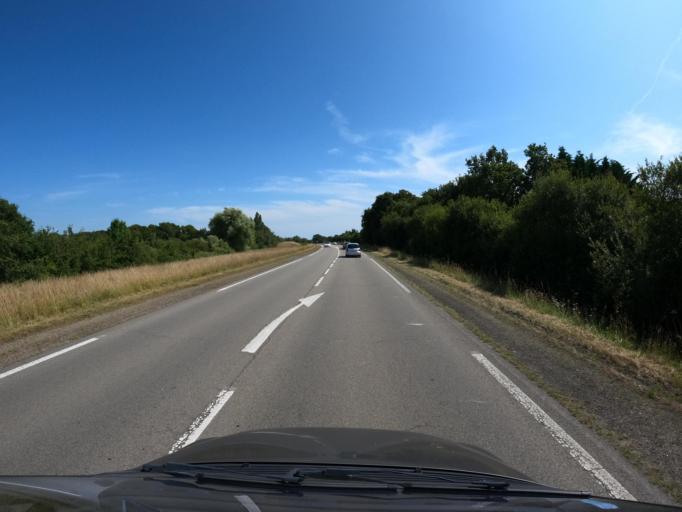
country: FR
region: Pays de la Loire
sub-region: Departement de la Loire-Atlantique
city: La Bernerie-en-Retz
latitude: 47.0932
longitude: -2.0348
